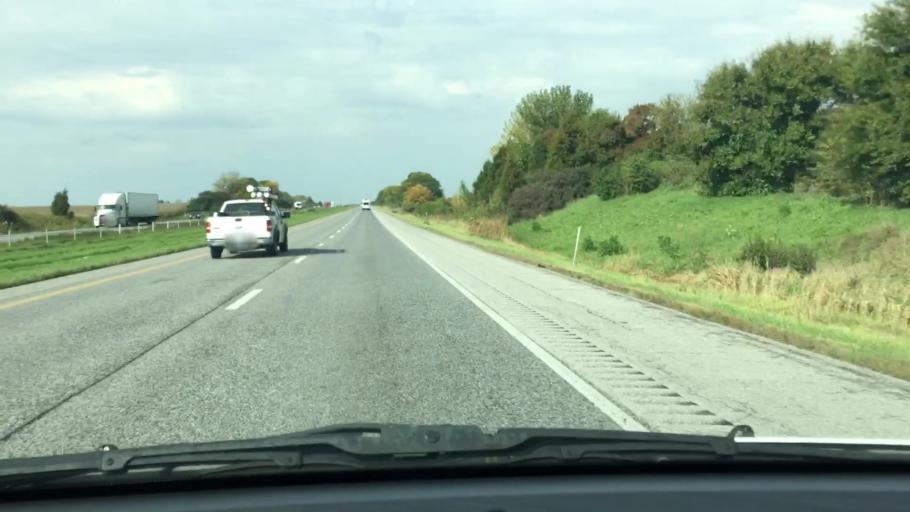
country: US
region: Illinois
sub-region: Rock Island County
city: Hampton
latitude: 41.5972
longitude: -90.3981
